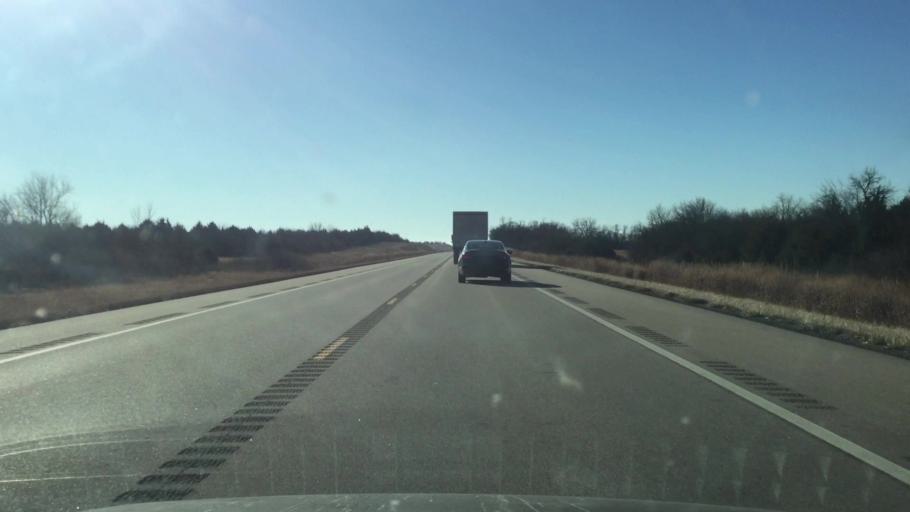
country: US
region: Kansas
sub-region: Allen County
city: Iola
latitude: 38.0369
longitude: -95.3806
